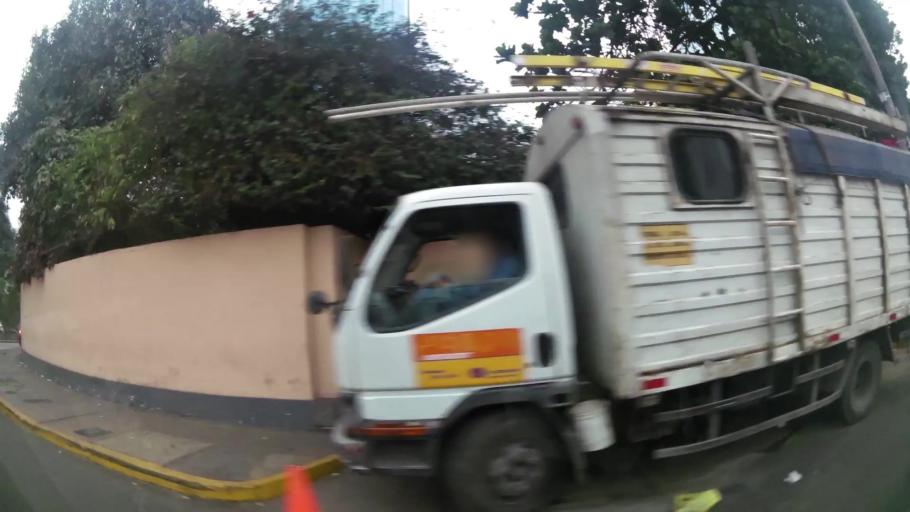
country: PE
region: Lima
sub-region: Lima
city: San Luis
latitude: -12.0911
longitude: -77.0239
